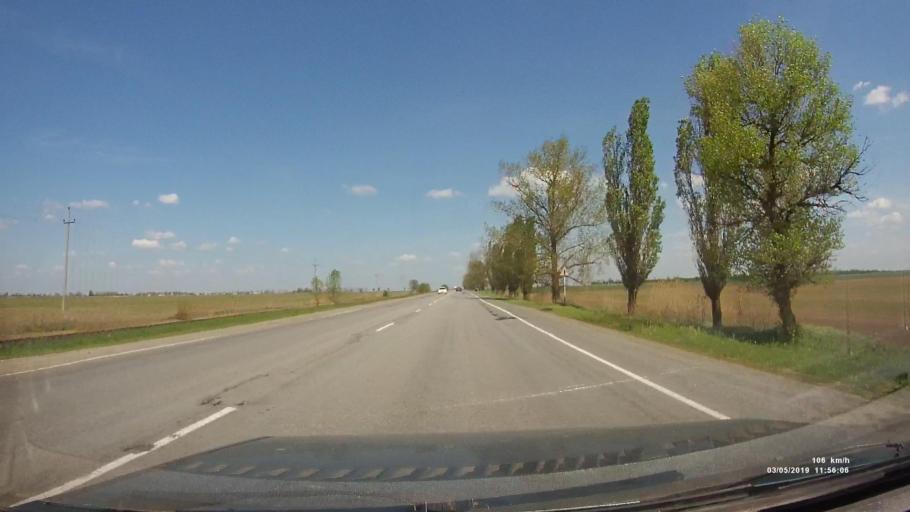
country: RU
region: Rostov
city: Bagayevskaya
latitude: 47.1900
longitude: 40.2977
